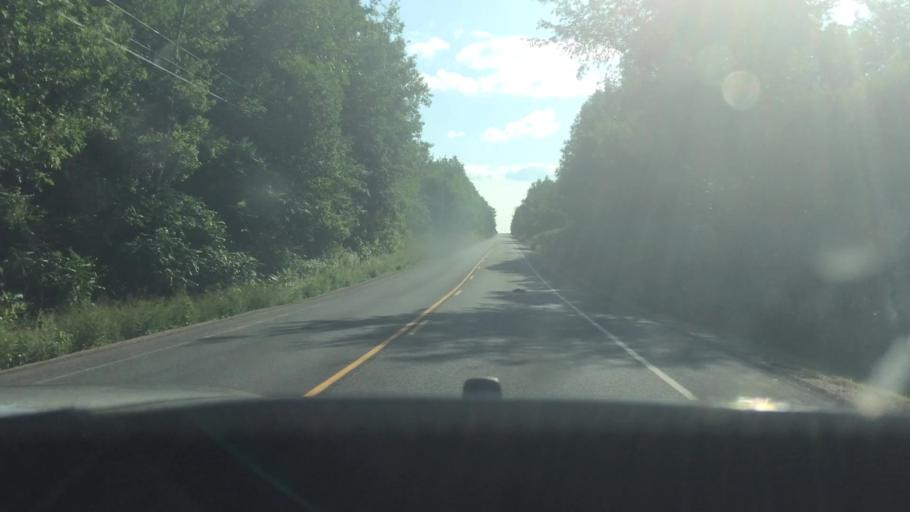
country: US
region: New York
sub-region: Franklin County
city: Malone
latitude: 44.7611
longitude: -74.5376
